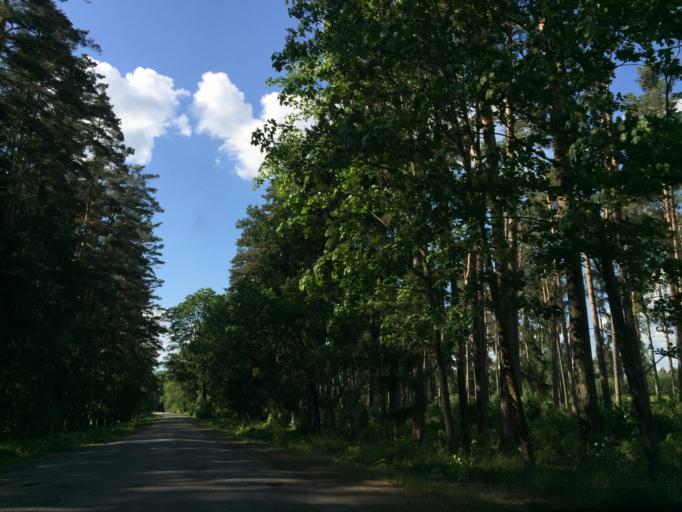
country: LV
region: Jaunpils
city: Jaunpils
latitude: 56.8716
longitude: 23.0023
